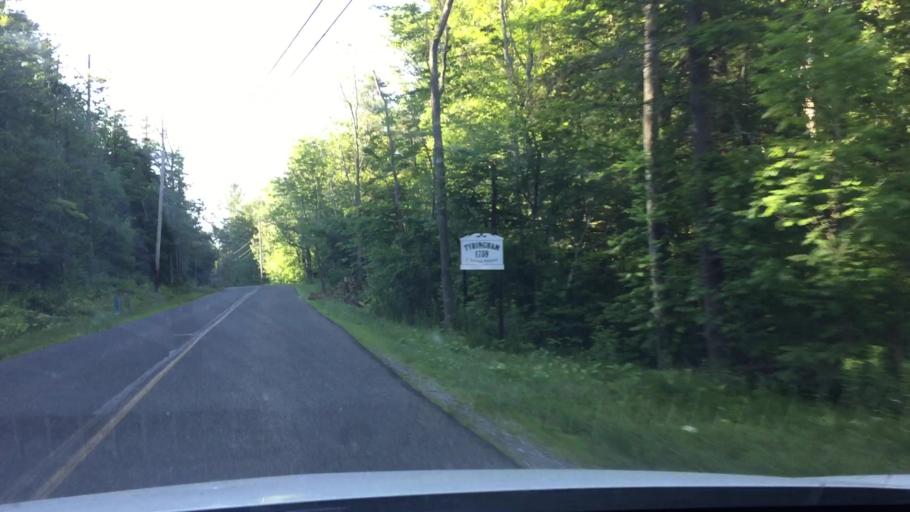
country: US
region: Massachusetts
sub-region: Berkshire County
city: Lee
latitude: 42.2800
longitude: -73.2098
